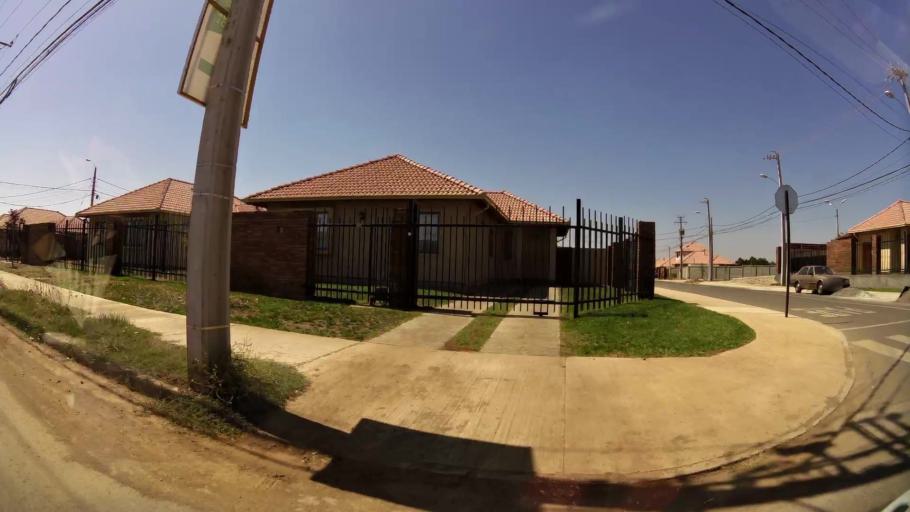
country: CL
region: Maule
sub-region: Provincia de Talca
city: Talca
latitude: -35.4355
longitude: -71.5928
